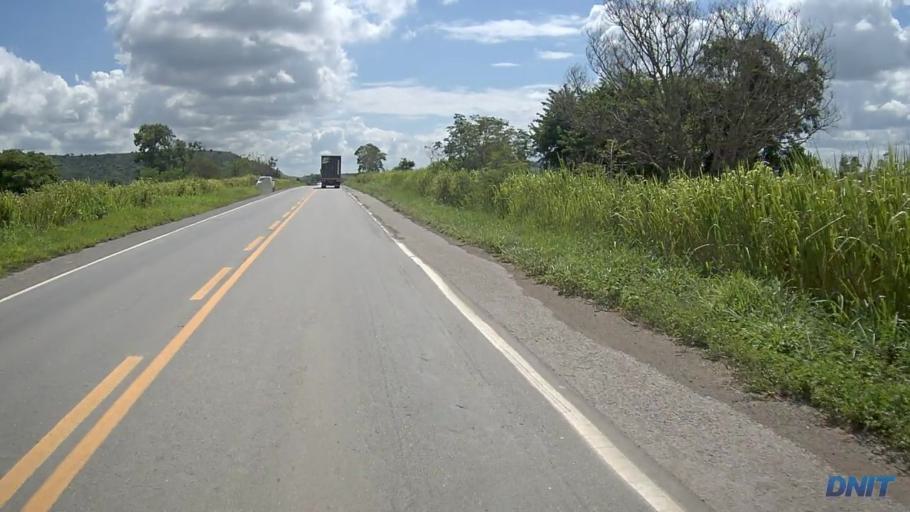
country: BR
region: Minas Gerais
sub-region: Governador Valadares
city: Governador Valadares
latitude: -19.0078
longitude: -42.1342
